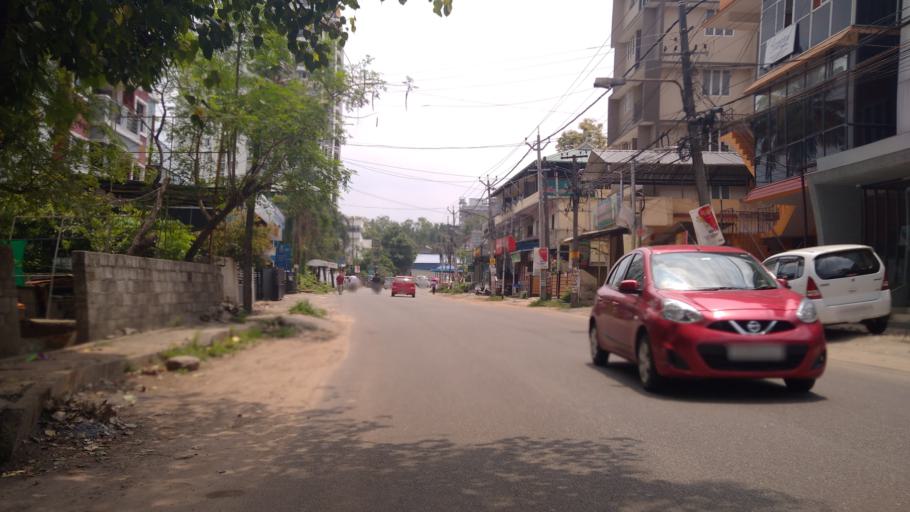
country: IN
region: Kerala
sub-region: Ernakulam
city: Elur
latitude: 10.0311
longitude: 76.3212
